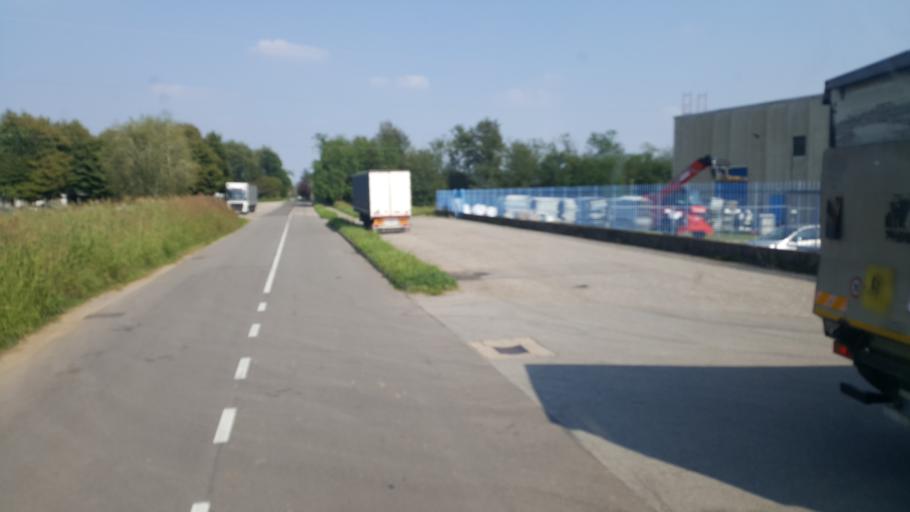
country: IT
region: Lombardy
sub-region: Provincia di Como
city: Locate Varesino
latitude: 45.6774
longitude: 8.9281
